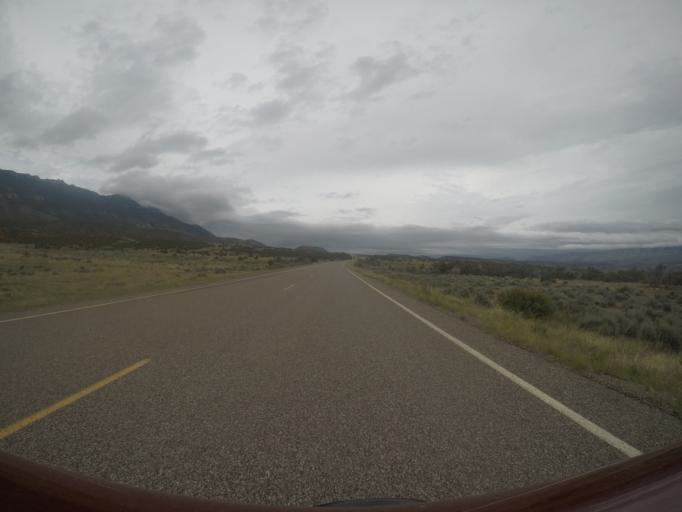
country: US
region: Wyoming
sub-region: Big Horn County
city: Lovell
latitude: 45.0886
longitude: -108.2511
